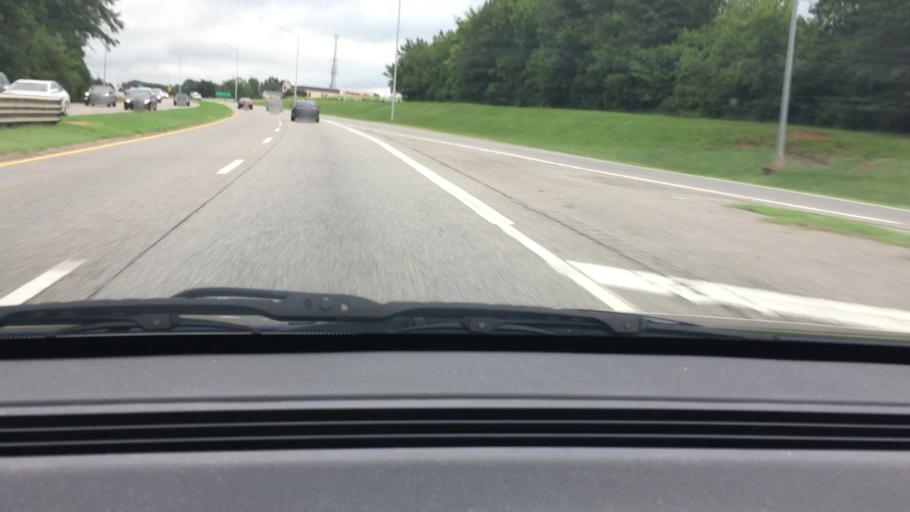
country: US
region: Alabama
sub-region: Tuscaloosa County
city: Tuscaloosa
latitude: 33.2082
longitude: -87.5242
